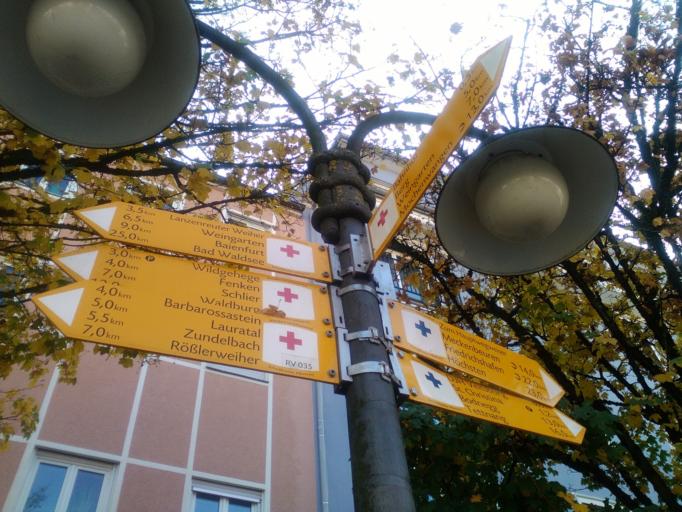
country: DE
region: Baden-Wuerttemberg
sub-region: Tuebingen Region
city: Ravensburg
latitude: 47.7828
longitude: 9.6135
